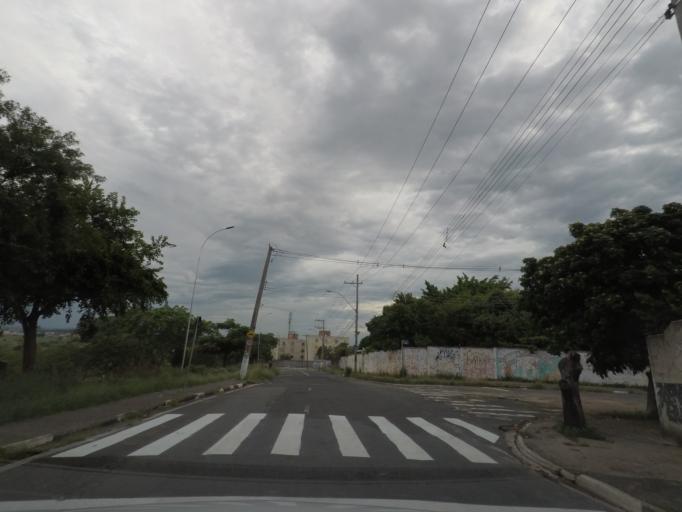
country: BR
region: Sao Paulo
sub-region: Hortolandia
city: Hortolandia
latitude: -22.9580
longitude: -47.1905
